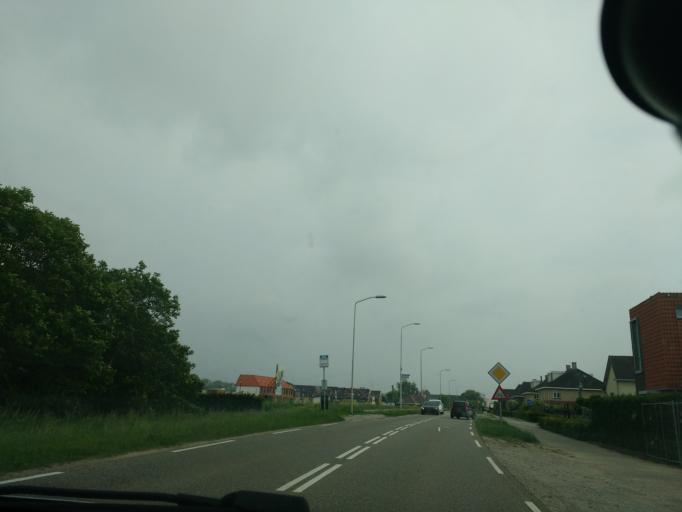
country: NL
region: Gelderland
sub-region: Gemeente Overbetuwe
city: Oosterhout
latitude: 51.8791
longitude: 5.8494
